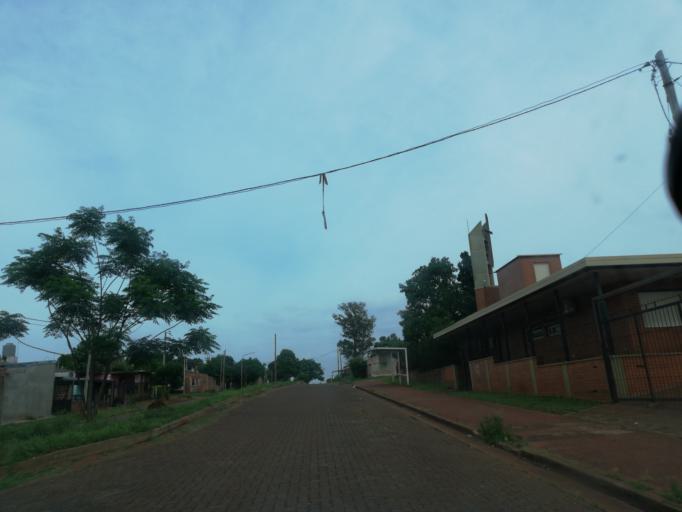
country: AR
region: Misiones
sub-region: Departamento de Capital
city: Posadas
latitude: -27.4367
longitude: -55.9068
